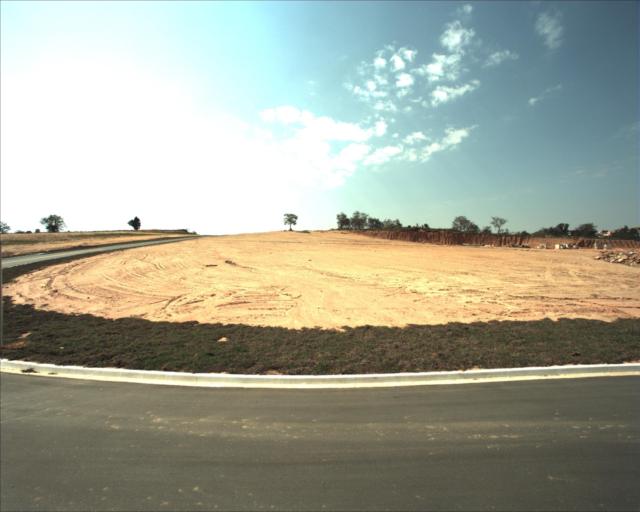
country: BR
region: Sao Paulo
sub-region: Sorocaba
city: Sorocaba
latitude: -23.4393
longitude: -47.4914
